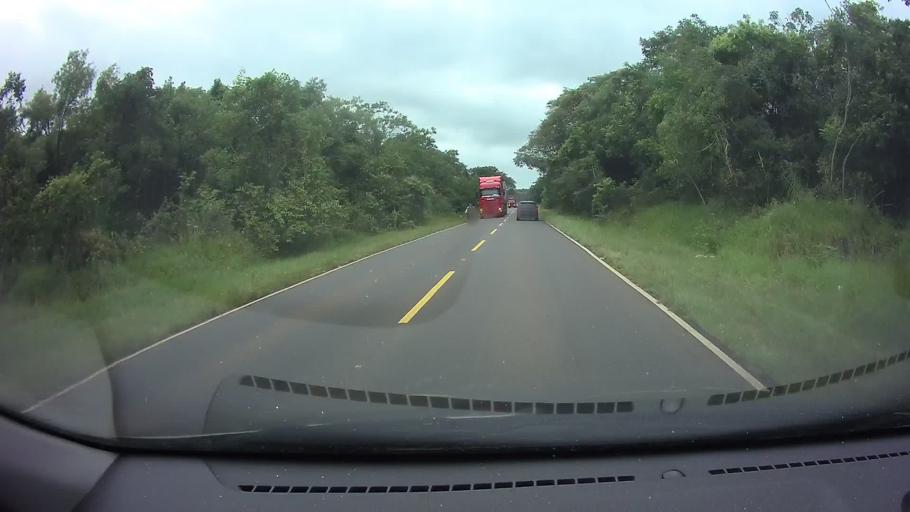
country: PY
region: Paraguari
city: Carapegua
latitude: -25.7308
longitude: -57.3080
